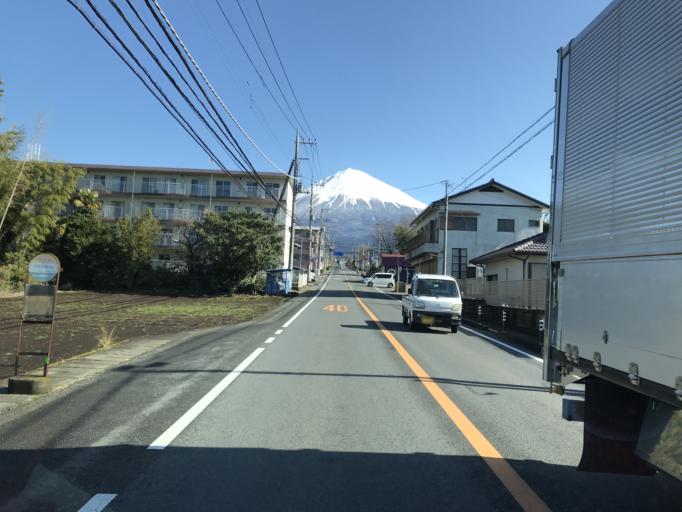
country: JP
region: Shizuoka
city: Fujinomiya
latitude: 35.2451
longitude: 138.6235
